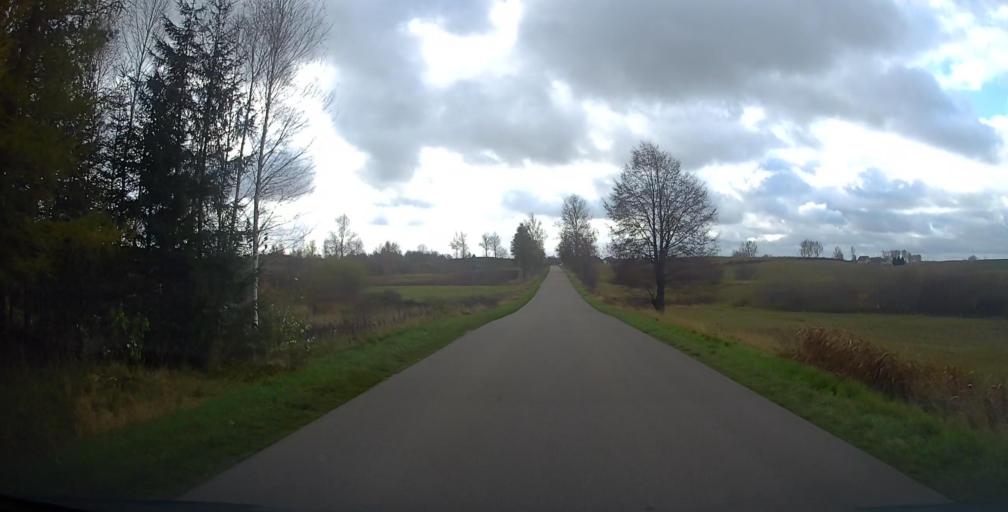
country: PL
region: Podlasie
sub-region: Suwalki
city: Suwalki
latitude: 54.3496
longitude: 22.8562
